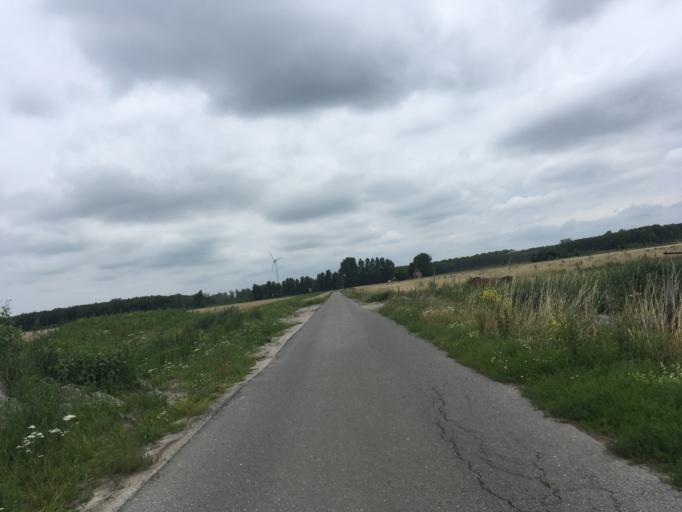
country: NL
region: North Holland
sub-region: Gemeente Velsen
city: Velsen-Zuid
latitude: 52.4198
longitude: 4.7241
